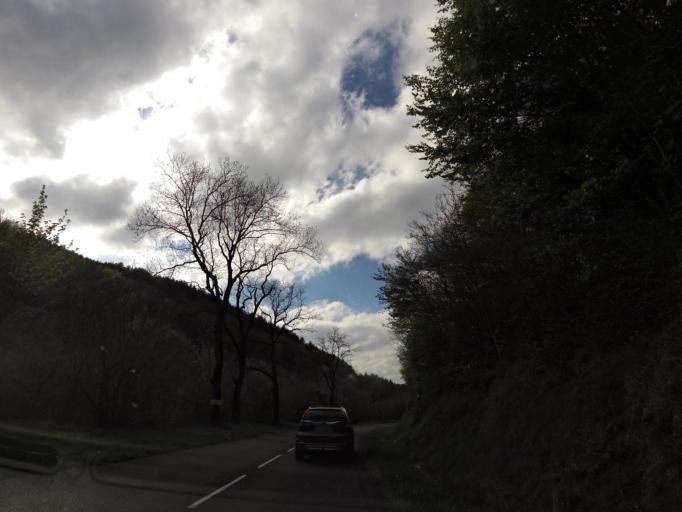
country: FR
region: Midi-Pyrenees
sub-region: Departement du Tarn
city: Soreze
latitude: 43.4195
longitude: 2.0605
